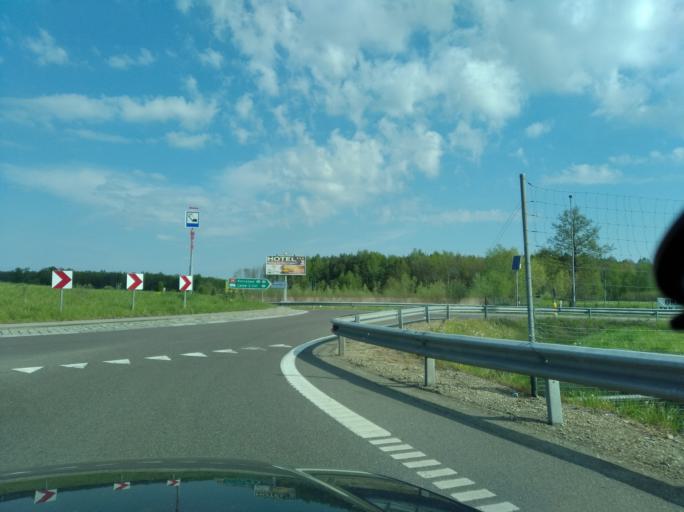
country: PL
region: Subcarpathian Voivodeship
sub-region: Powiat lubaczowski
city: Wielkie Oczy
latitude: 49.9664
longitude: 23.0678
